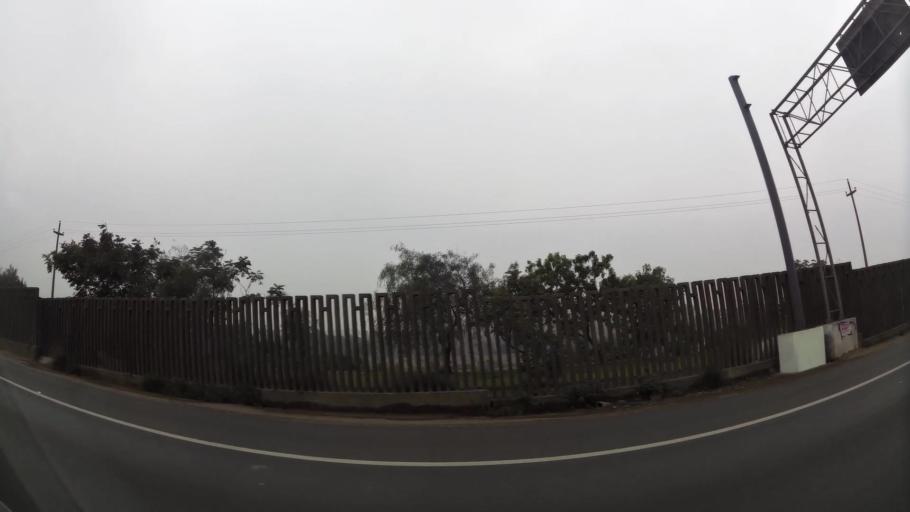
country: PE
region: Lima
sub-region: Lima
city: Vitarte
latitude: -12.0206
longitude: -76.9195
